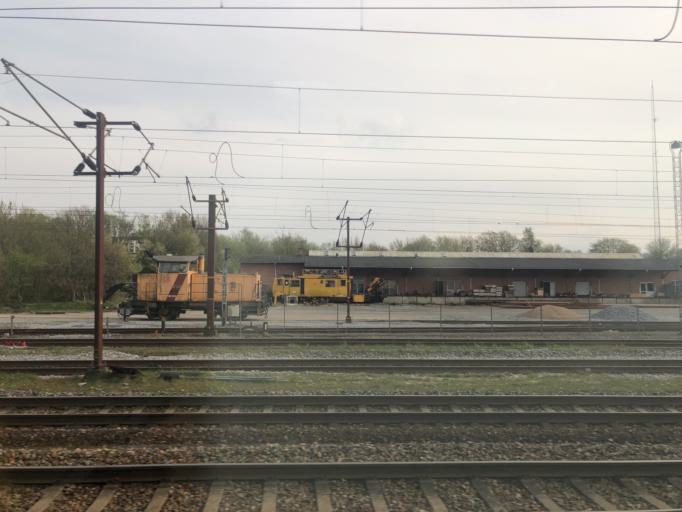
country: DK
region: Zealand
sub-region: Ringsted Kommune
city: Ringsted
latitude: 55.4382
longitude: 11.7902
